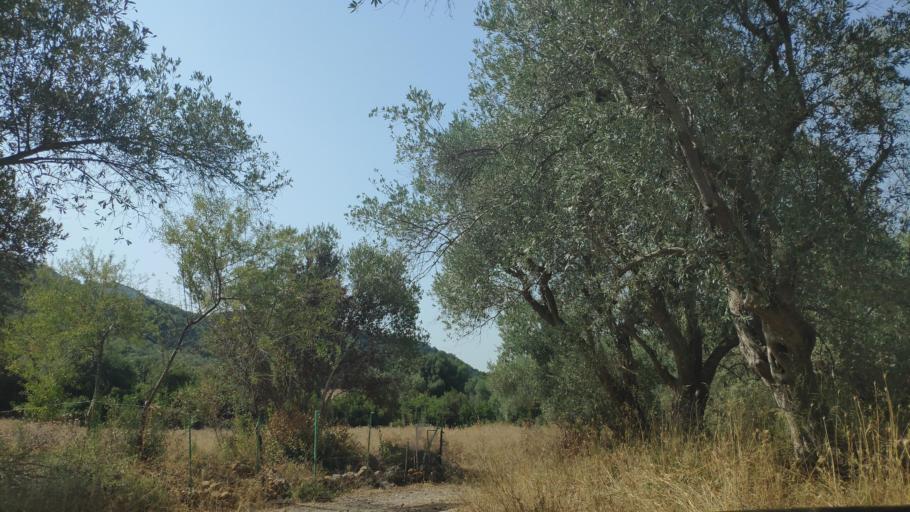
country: GR
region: West Greece
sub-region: Nomos Aitolias kai Akarnanias
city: Fitiai
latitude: 38.7261
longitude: 21.1884
